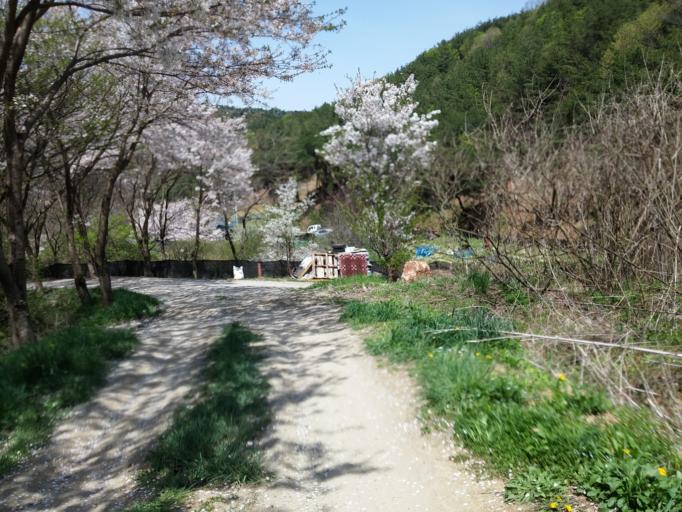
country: KR
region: Daejeon
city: Daejeon
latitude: 36.2789
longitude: 127.4787
